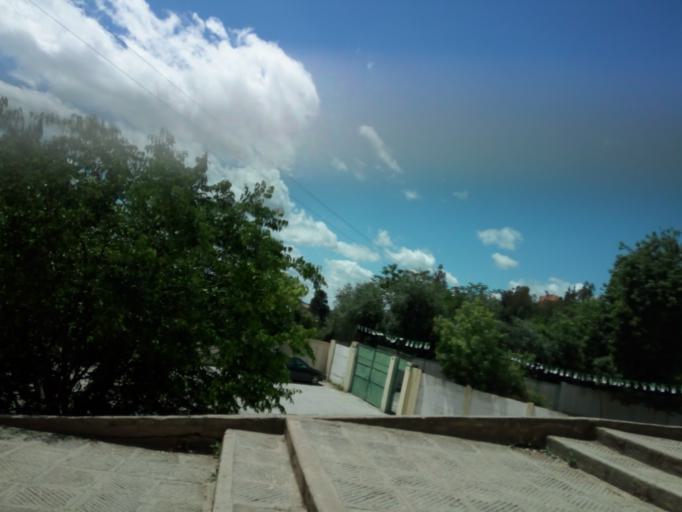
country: DZ
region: Constantine
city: Constantine
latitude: 36.3730
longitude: 6.6205
